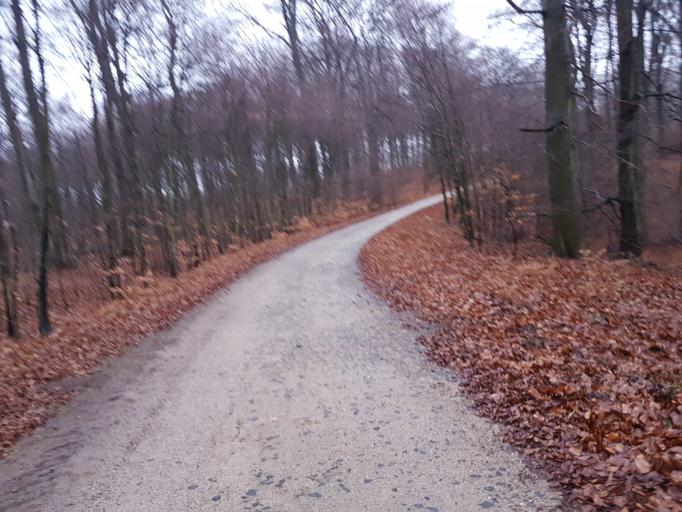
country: DE
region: Mecklenburg-Vorpommern
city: Ostseebad Binz
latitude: 54.3918
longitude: 13.6517
